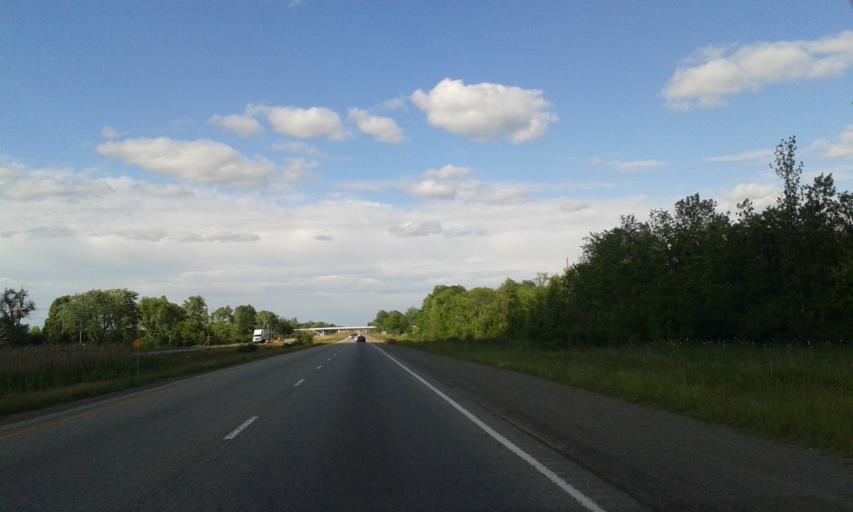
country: CA
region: Ontario
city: Prescott
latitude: 44.6908
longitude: -75.5805
